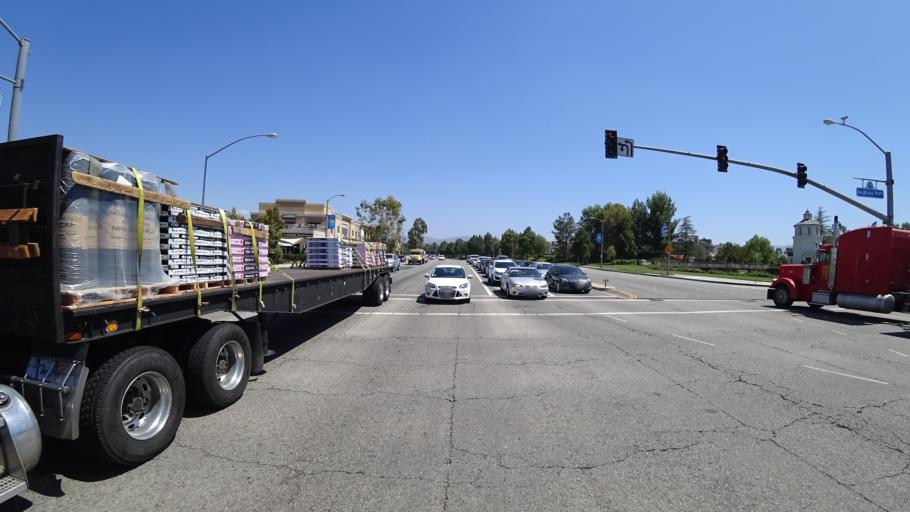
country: US
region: California
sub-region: Los Angeles County
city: Santa Clarita
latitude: 34.4313
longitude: -118.5574
